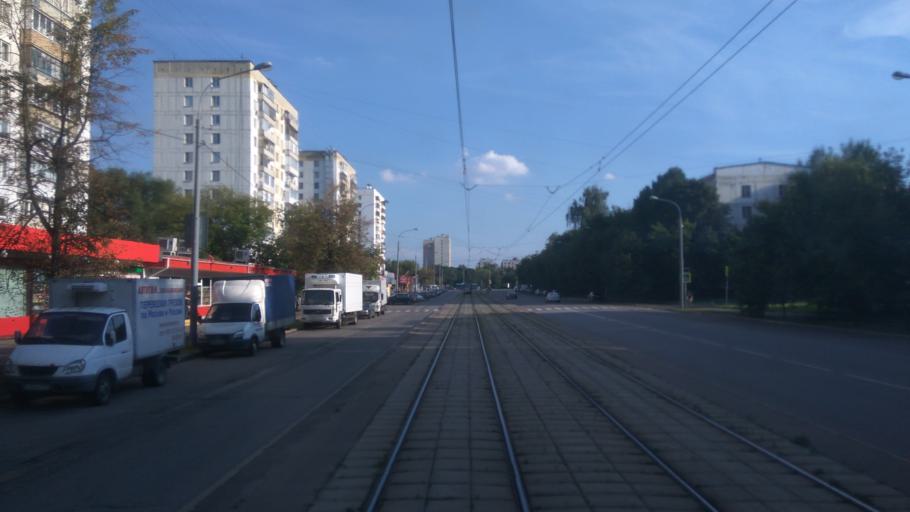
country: RU
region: Moscow
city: Perovo
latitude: 55.7549
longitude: 37.7901
